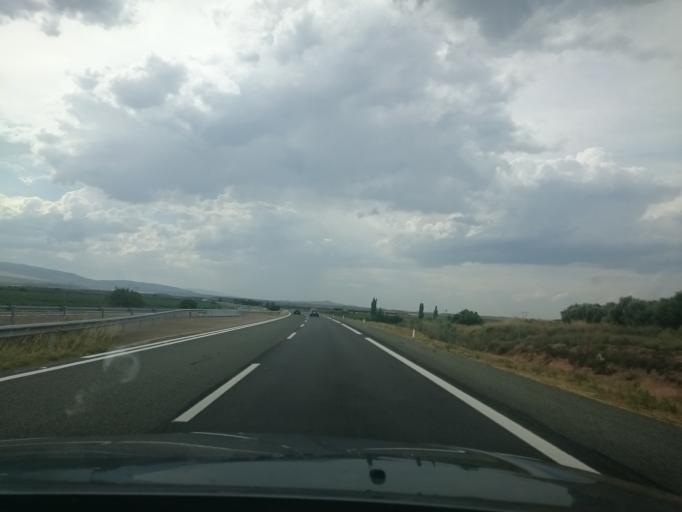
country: ES
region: Navarre
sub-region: Provincia de Navarra
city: Corella
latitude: 42.1484
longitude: -1.7902
